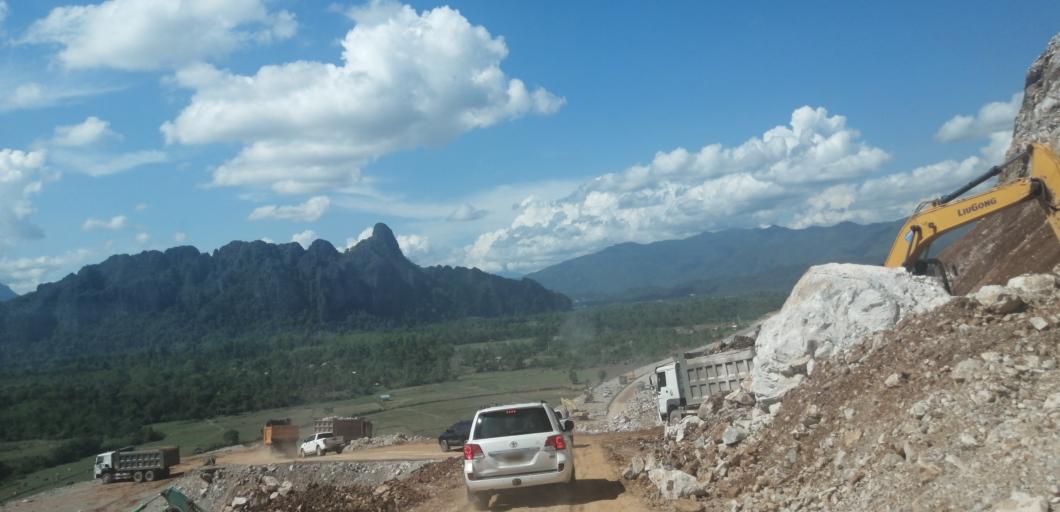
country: LA
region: Vientiane
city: Vangviang
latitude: 18.8707
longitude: 102.4283
